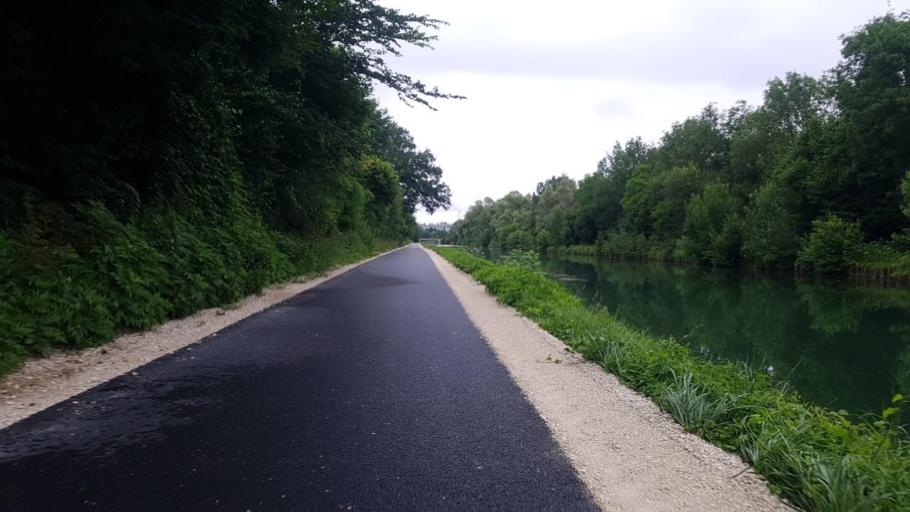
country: FR
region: Champagne-Ardenne
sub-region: Departement de la Marne
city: Vitry-le-Francois
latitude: 48.8277
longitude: 4.5140
